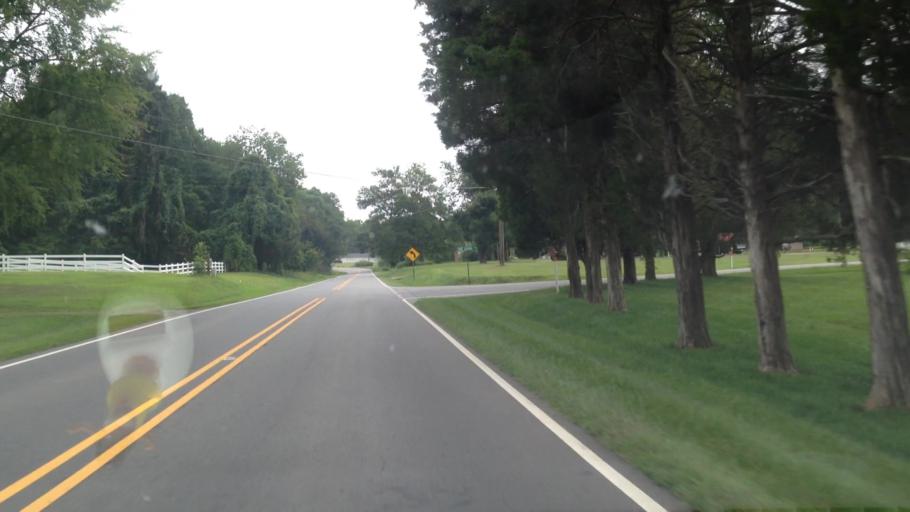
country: US
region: North Carolina
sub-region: Rockingham County
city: Mayodan
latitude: 36.4114
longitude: -80.0062
